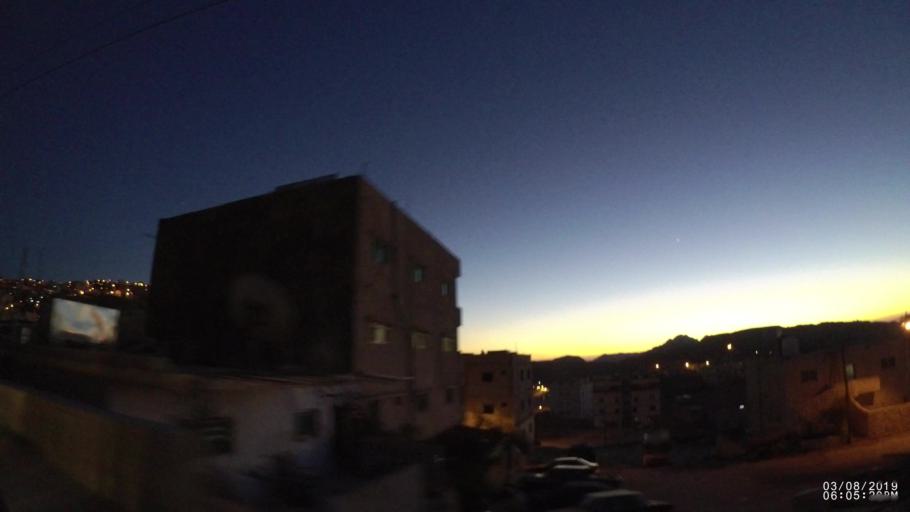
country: JO
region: Ma'an
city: Petra
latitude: 30.3280
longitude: 35.4716
